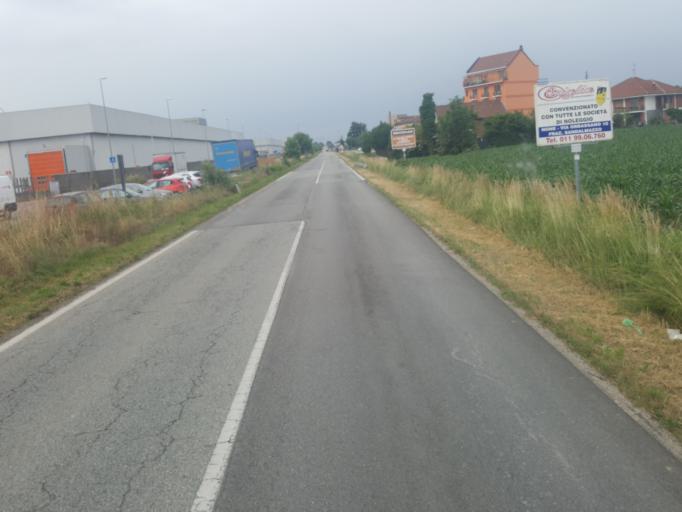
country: IT
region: Piedmont
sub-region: Provincia di Torino
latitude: 44.9475
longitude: 7.5469
